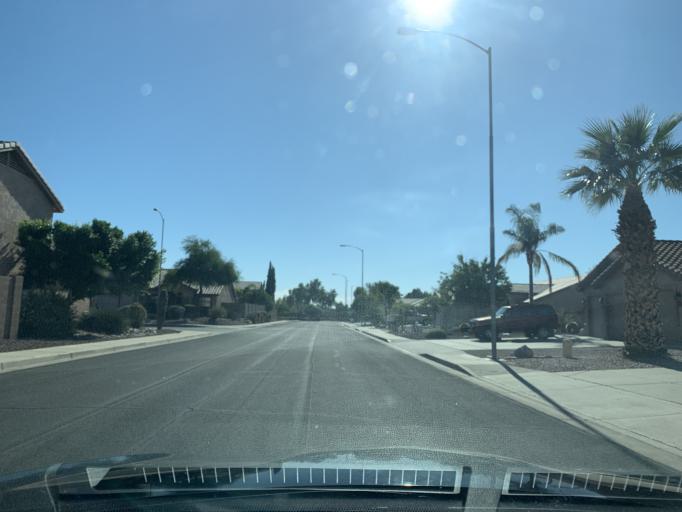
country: US
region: Arizona
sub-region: Pinal County
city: Apache Junction
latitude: 33.3808
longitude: -111.6232
